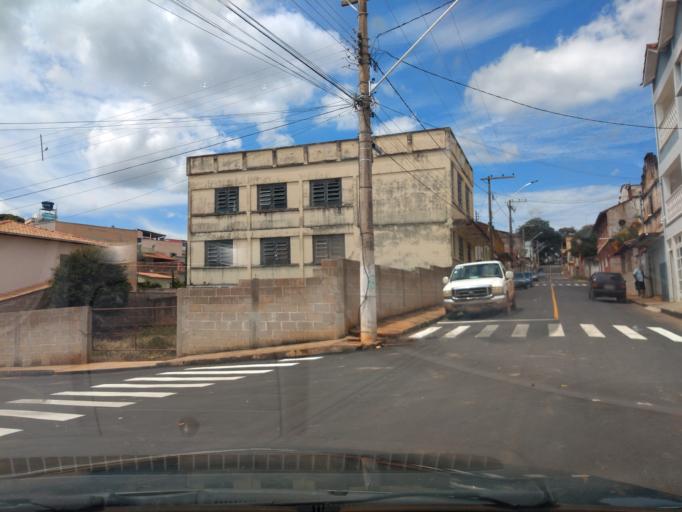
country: BR
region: Minas Gerais
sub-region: Lavras
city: Lavras
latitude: -21.5128
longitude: -44.9053
